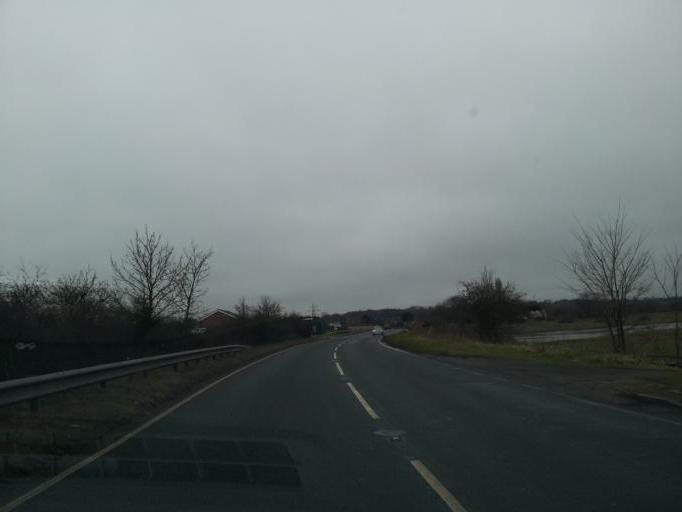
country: GB
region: England
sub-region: Essex
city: Manningtree
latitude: 51.9542
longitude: 1.0552
